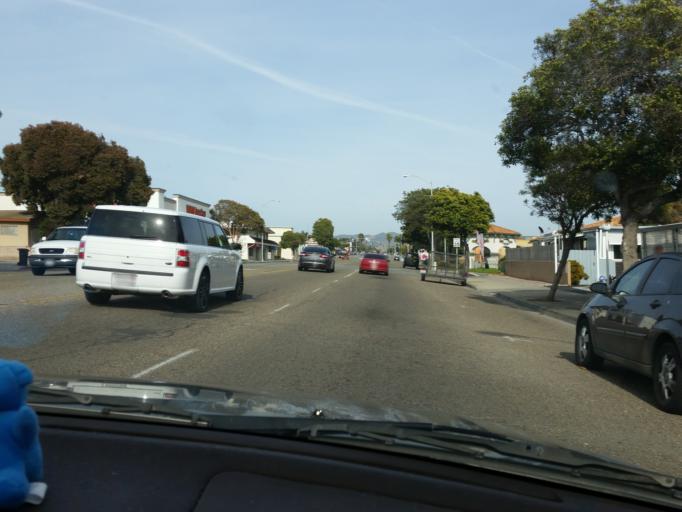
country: US
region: California
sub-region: San Luis Obispo County
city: Grover Beach
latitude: 35.1212
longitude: -120.6149
